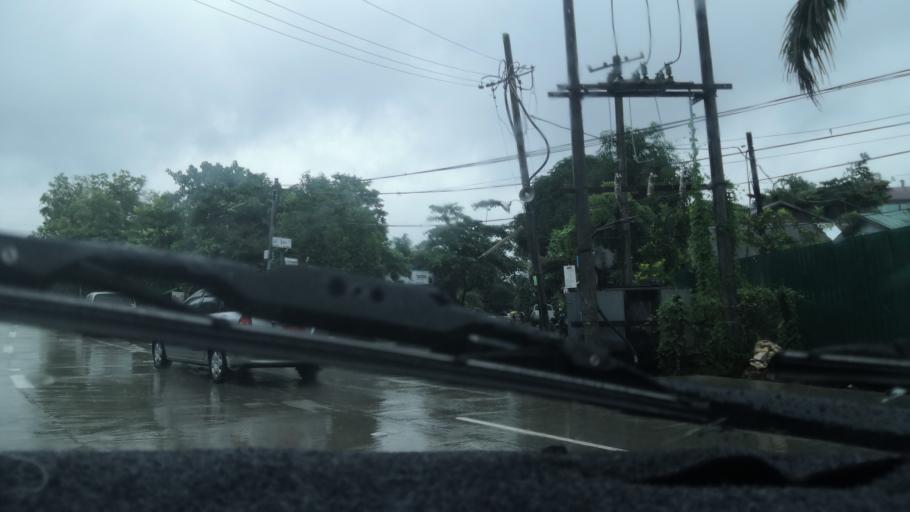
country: MM
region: Yangon
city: Yangon
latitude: 16.8882
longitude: 96.1498
